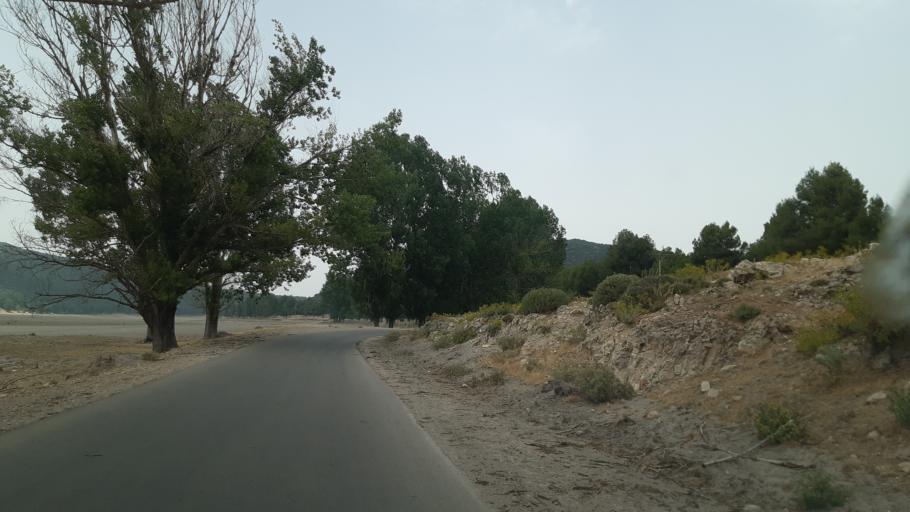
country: MA
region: Meknes-Tafilalet
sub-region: Ifrane
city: Ifrane
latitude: 33.6520
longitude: -5.0249
